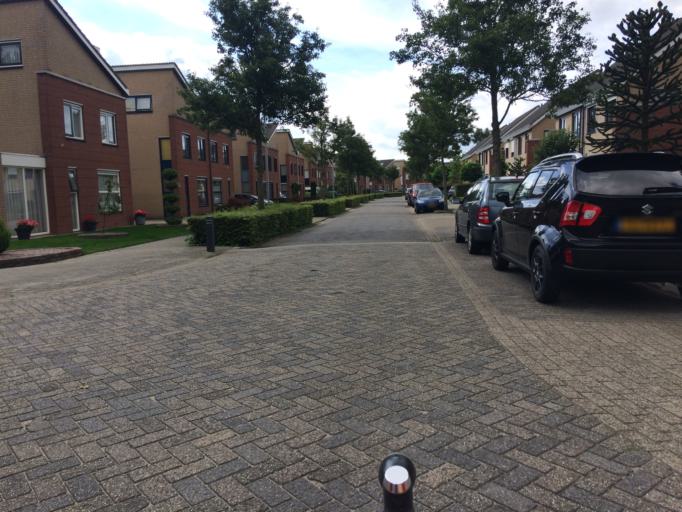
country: NL
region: Gelderland
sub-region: Gemeente Maasdriel
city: Hedel
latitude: 51.7327
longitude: 5.2879
